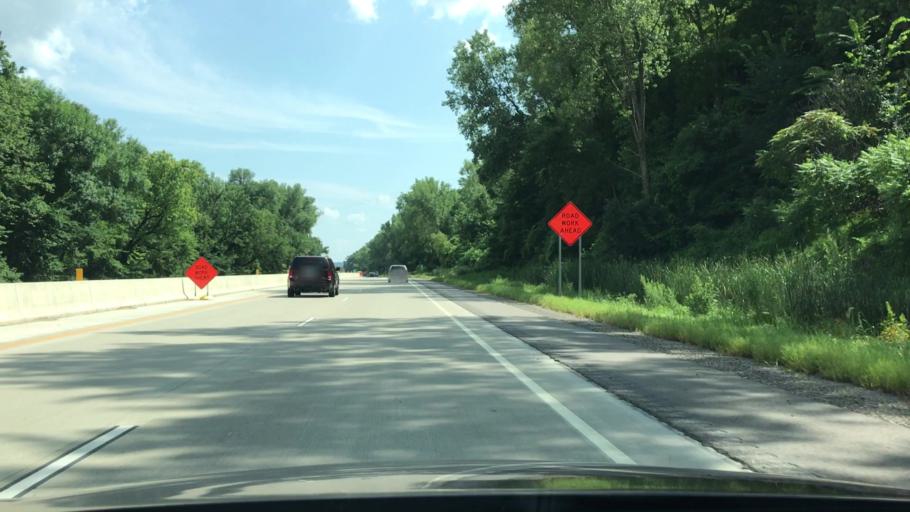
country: US
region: Minnesota
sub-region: Nicollet County
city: North Mankato
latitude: 44.2114
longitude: -94.0265
